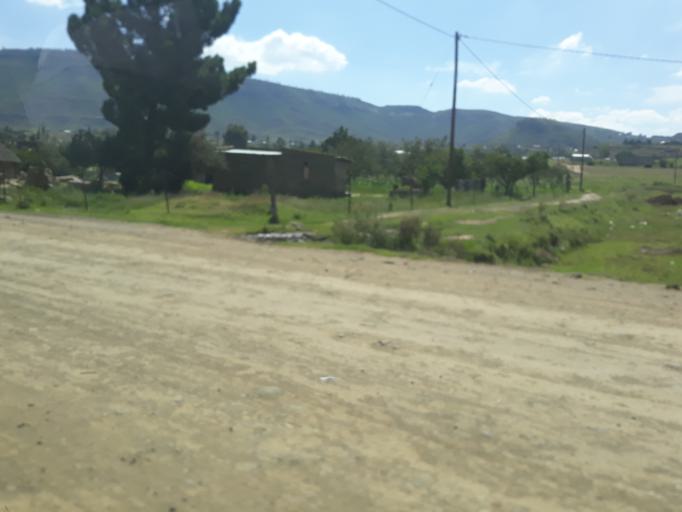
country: LS
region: Mohale's Hoek District
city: Mohale's Hoek
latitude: -30.1116
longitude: 27.4700
